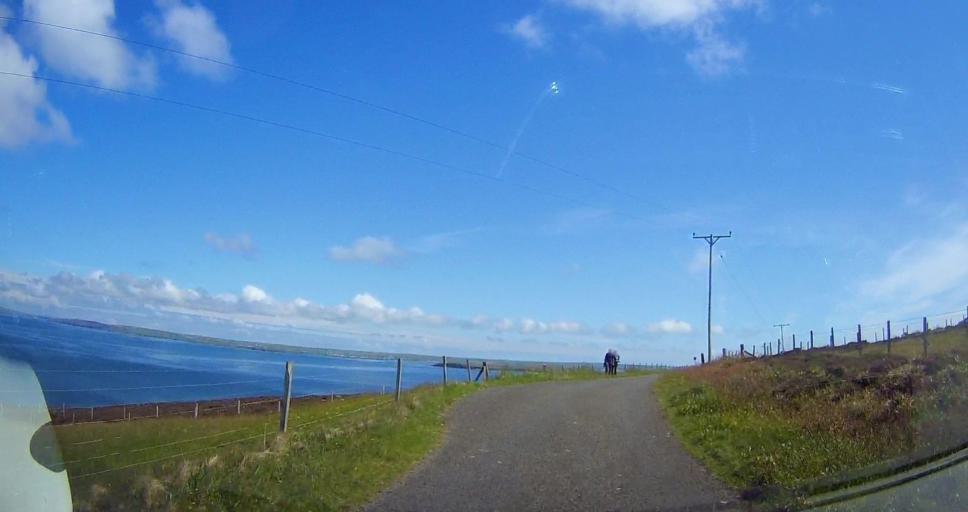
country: GB
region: Scotland
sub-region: Orkney Islands
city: Orkney
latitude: 58.8547
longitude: -2.9503
